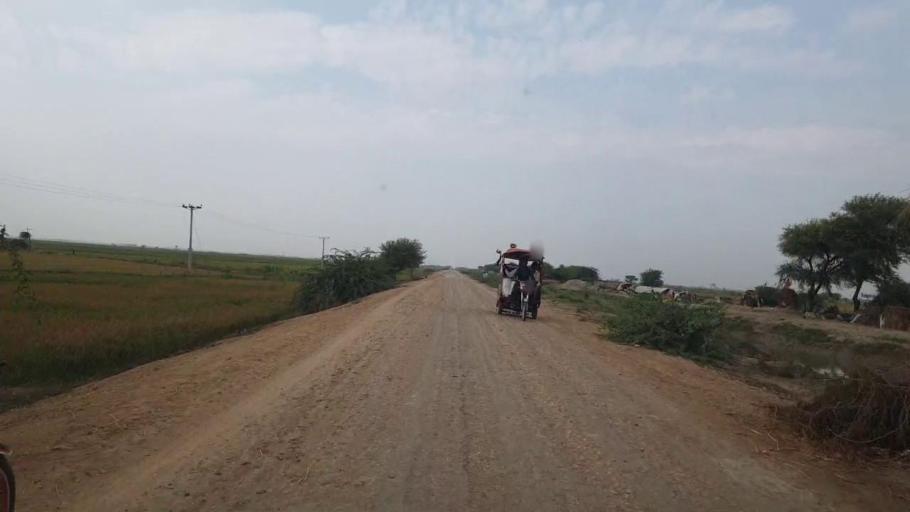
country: PK
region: Sindh
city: Kario
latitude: 24.6105
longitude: 68.5925
